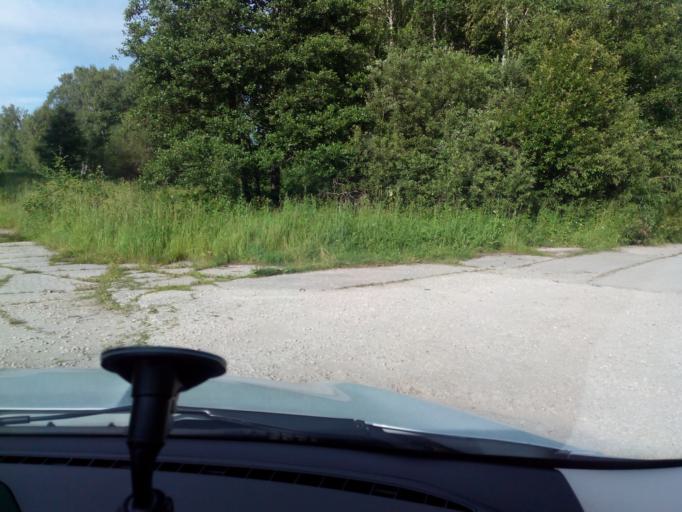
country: RU
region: Vladimir
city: Petushki
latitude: 56.0376
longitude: 39.4936
